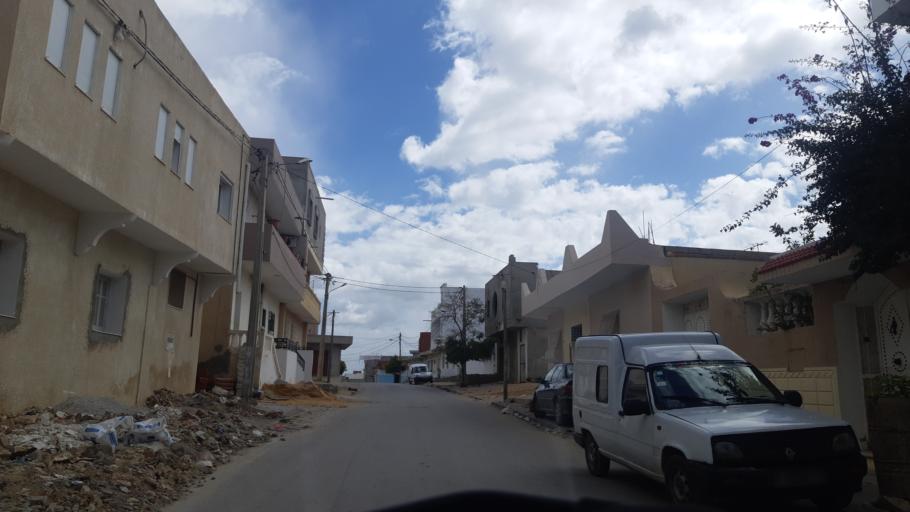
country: TN
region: Susah
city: Akouda
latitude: 35.8619
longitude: 10.5403
